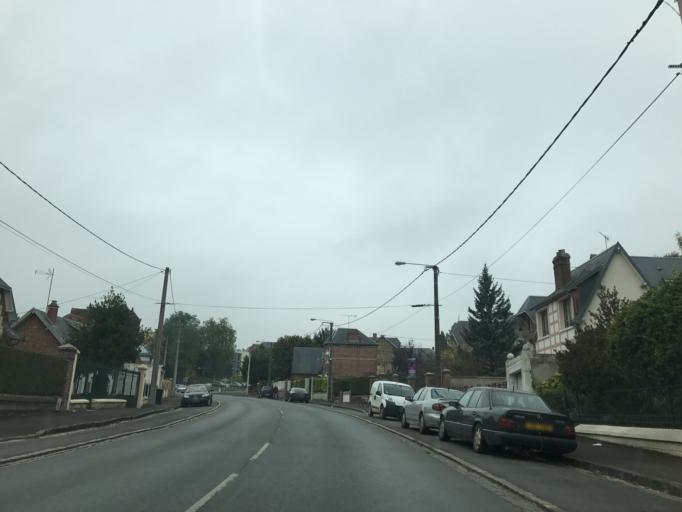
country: FR
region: Picardie
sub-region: Departement de la Somme
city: Peronne
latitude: 49.9318
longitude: 2.9319
